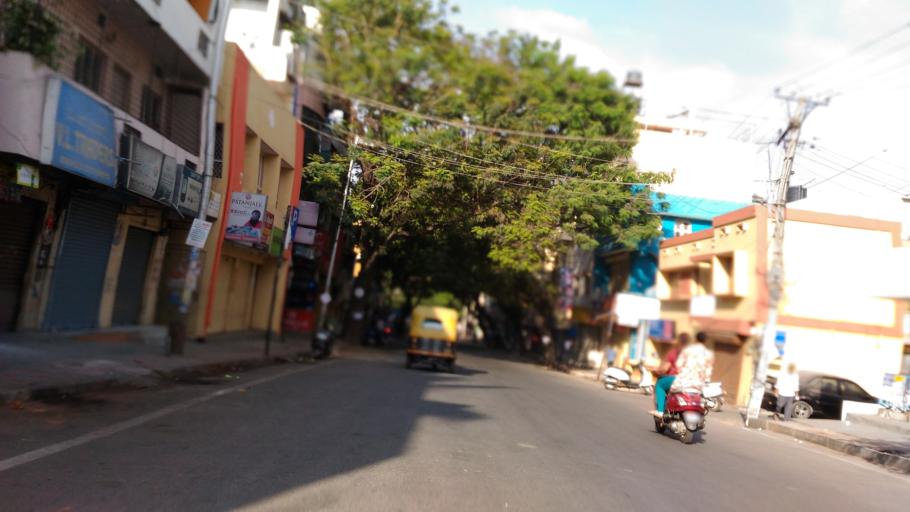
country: IN
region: Karnataka
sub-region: Bangalore Urban
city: Bangalore
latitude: 12.9417
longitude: 77.5628
